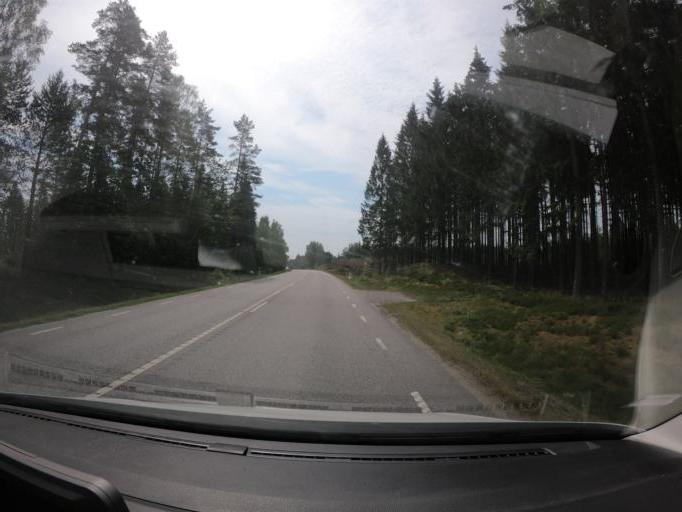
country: SE
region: Skane
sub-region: Hassleholms Kommun
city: Bjarnum
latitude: 56.2322
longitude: 13.7146
